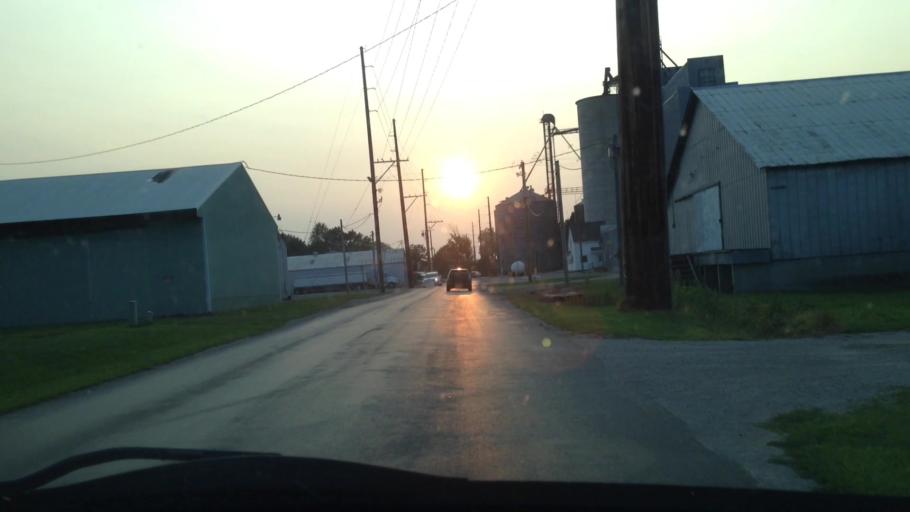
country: US
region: Iowa
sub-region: Linn County
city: Palo
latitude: 42.0917
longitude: -91.8702
